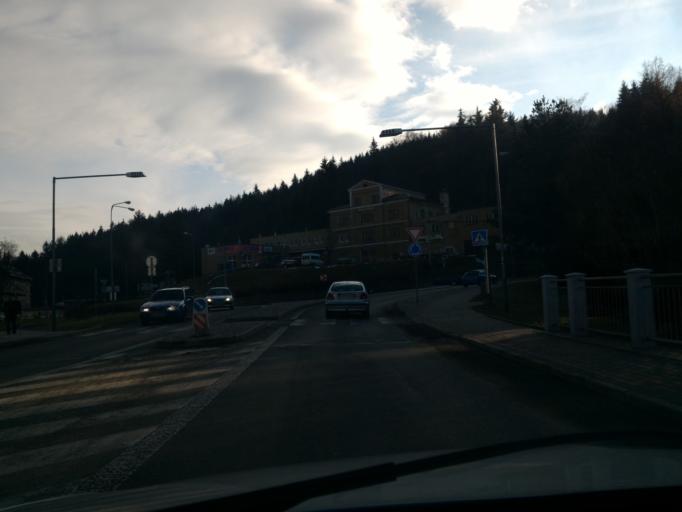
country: CZ
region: Liberecky
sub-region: Okres Jablonec nad Nisou
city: Tanvald
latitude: 50.7360
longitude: 15.3081
